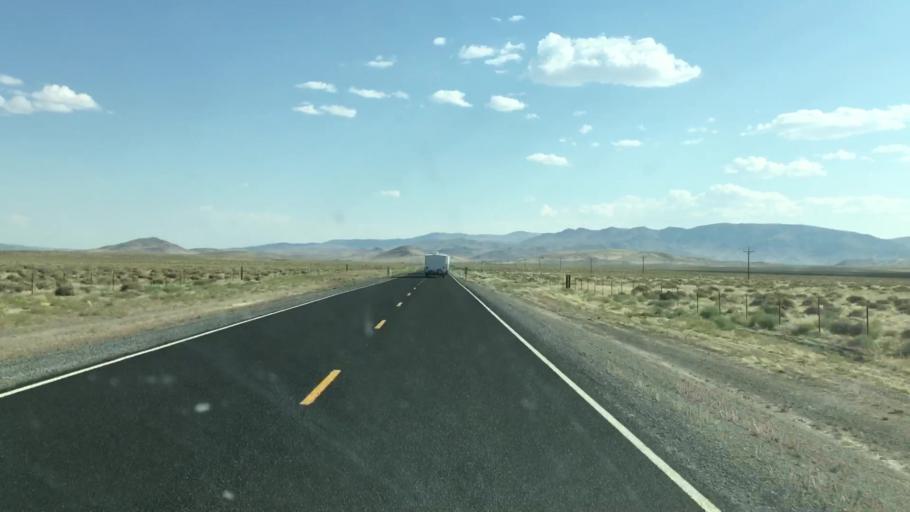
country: US
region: Nevada
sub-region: Lyon County
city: Fernley
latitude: 39.6732
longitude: -119.3327
